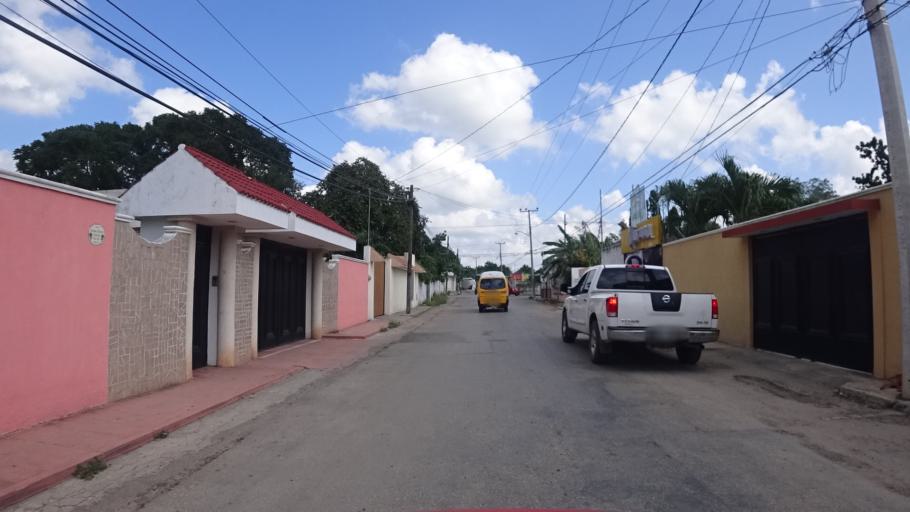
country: MX
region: Yucatan
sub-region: Tizimin
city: Tizimin
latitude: 21.1528
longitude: -88.1506
